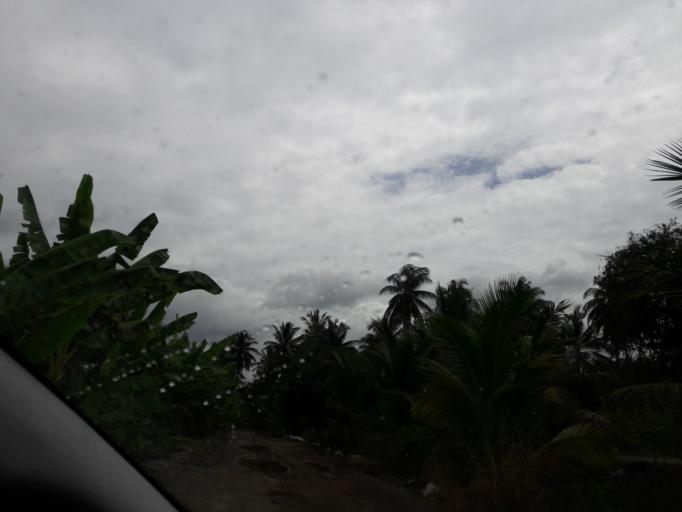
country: TH
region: Ratchaburi
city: Damnoen Saduak
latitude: 13.5250
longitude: 99.9453
